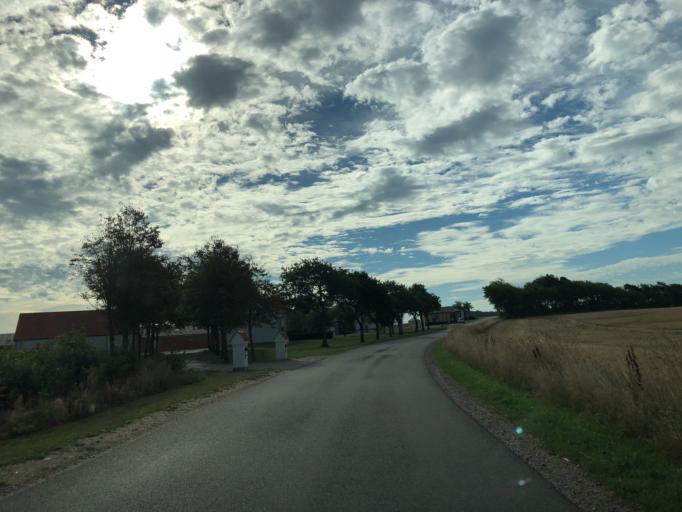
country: DK
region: Central Jutland
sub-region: Ringkobing-Skjern Kommune
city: Skjern
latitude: 56.1093
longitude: 8.4266
